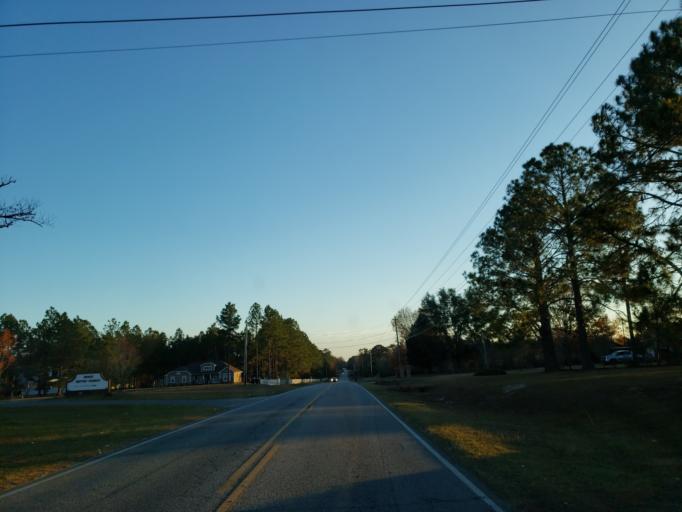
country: US
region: Georgia
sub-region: Crisp County
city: Cordele
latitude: 31.9432
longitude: -83.7659
